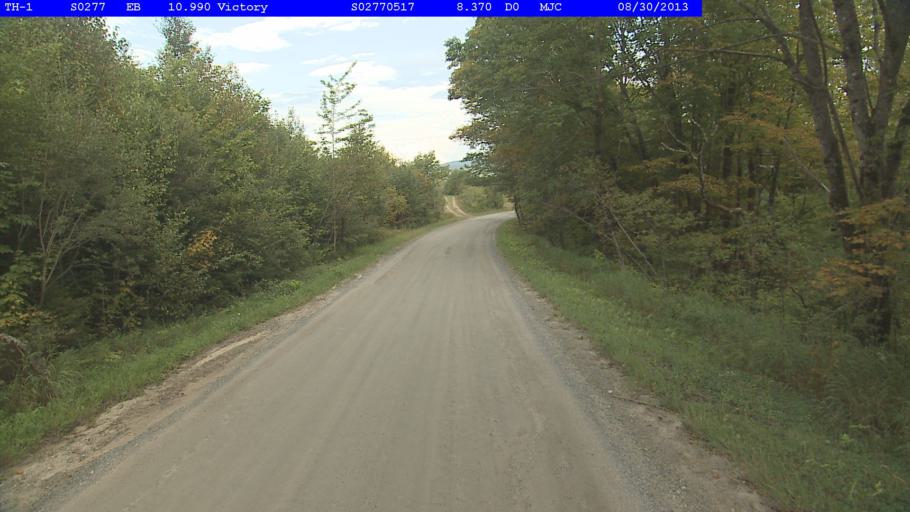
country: US
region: Vermont
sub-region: Essex County
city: Guildhall
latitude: 44.5700
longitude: -71.7681
